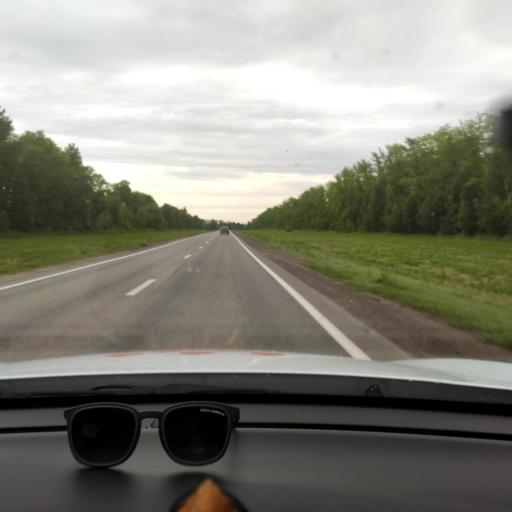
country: RU
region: Tatarstan
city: Pestretsy
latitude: 55.8334
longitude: 49.6331
